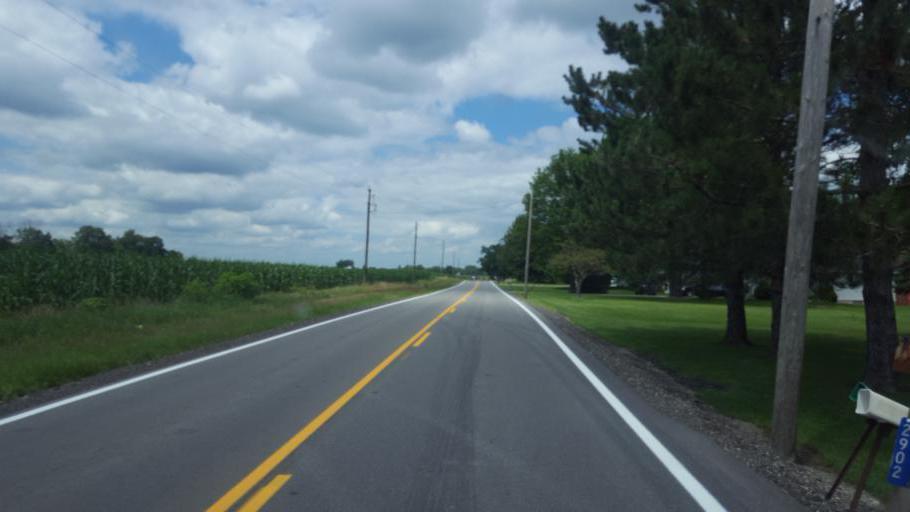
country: US
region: Ohio
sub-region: Richland County
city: Shelby
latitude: 40.8330
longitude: -82.6556
